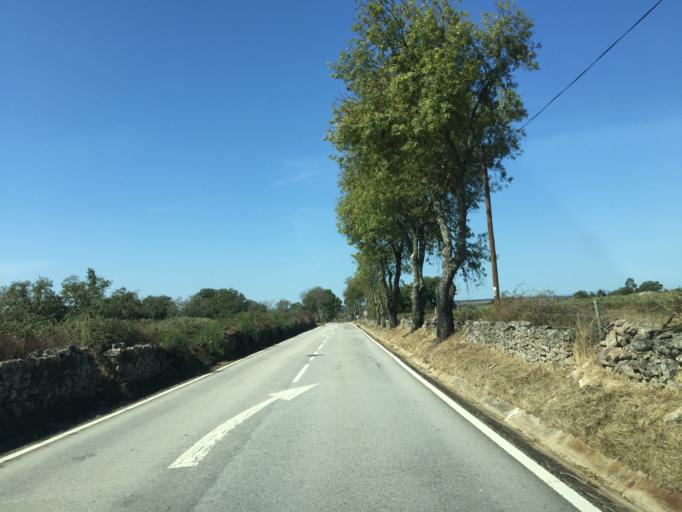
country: PT
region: Portalegre
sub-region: Portalegre
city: Alagoa
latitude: 39.4394
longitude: -7.5590
